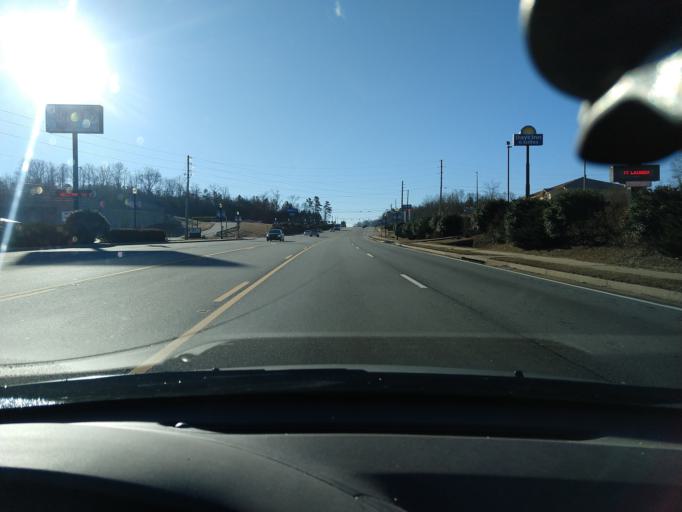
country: US
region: Georgia
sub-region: Jackson County
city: Commerce
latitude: 34.2484
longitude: -83.4599
